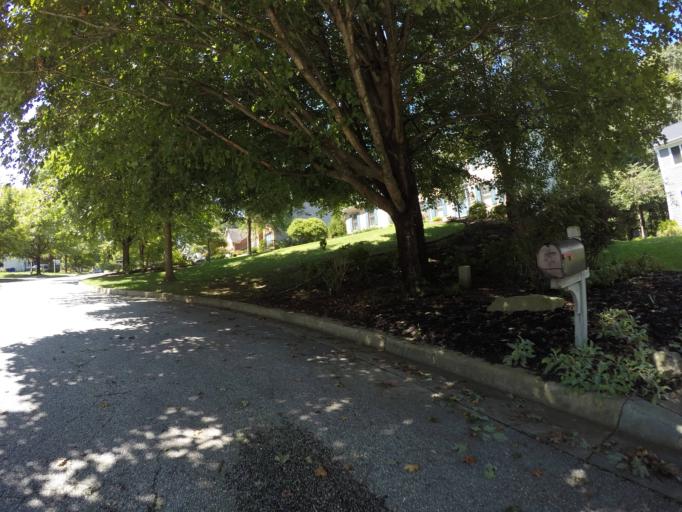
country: US
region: Maryland
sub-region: Howard County
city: Columbia
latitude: 39.2932
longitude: -76.8815
